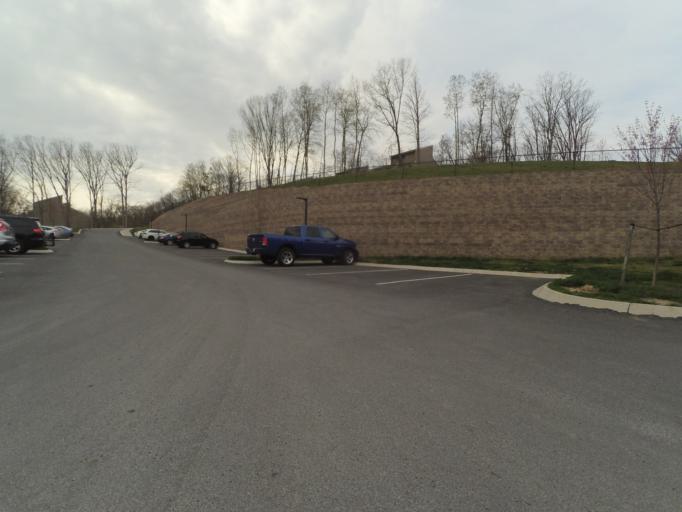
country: US
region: Pennsylvania
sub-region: Centre County
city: Park Forest Village
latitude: 40.8225
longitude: -77.8894
